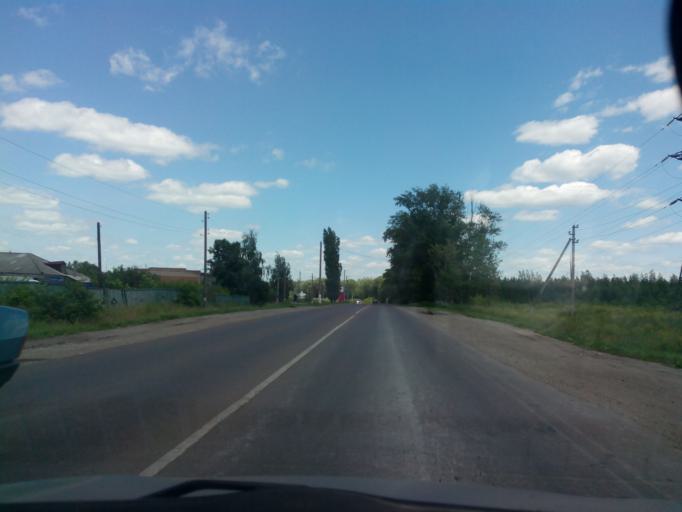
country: RU
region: Tambov
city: Zherdevka
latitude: 51.8332
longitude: 41.4996
